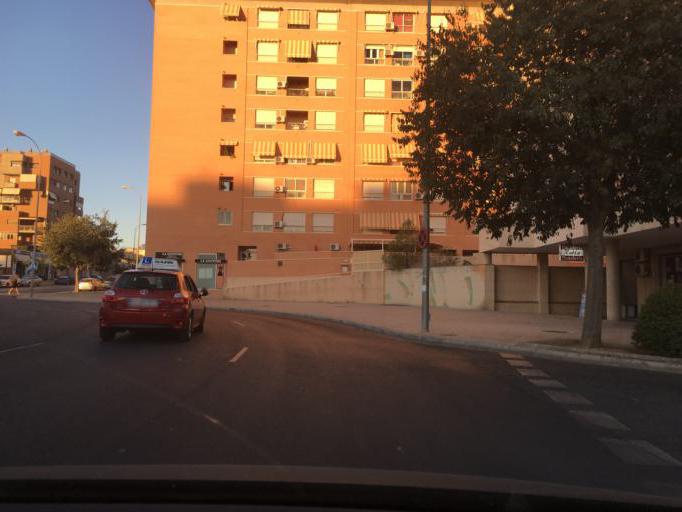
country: ES
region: Andalusia
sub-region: Provincia de Granada
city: Granada
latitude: 37.1995
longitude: -3.6168
